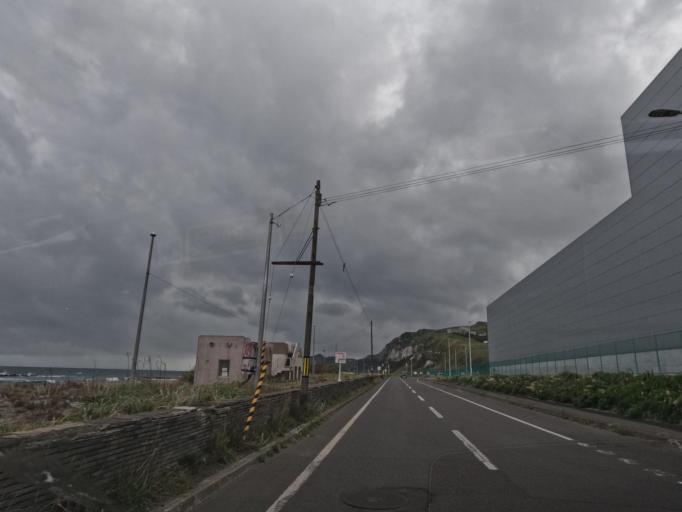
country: JP
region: Hokkaido
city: Muroran
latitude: 42.3338
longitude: 141.0239
